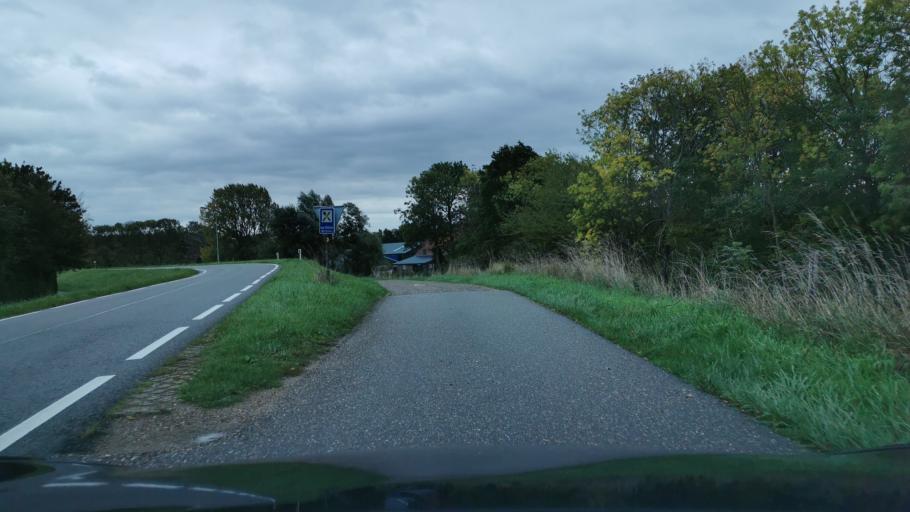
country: NL
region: Zeeland
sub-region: Gemeente Veere
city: Veere
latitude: 51.5575
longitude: 3.6471
